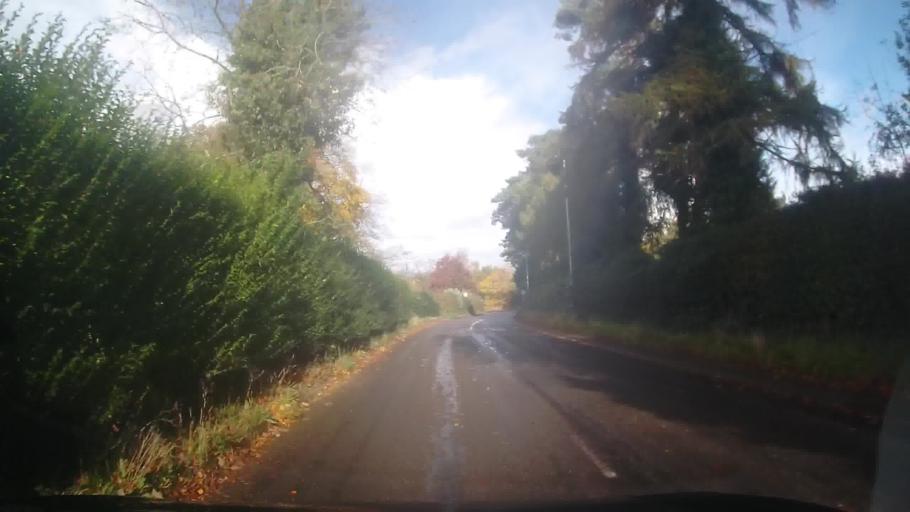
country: GB
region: England
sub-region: Shropshire
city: Whitchurch
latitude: 52.9606
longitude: -2.6785
